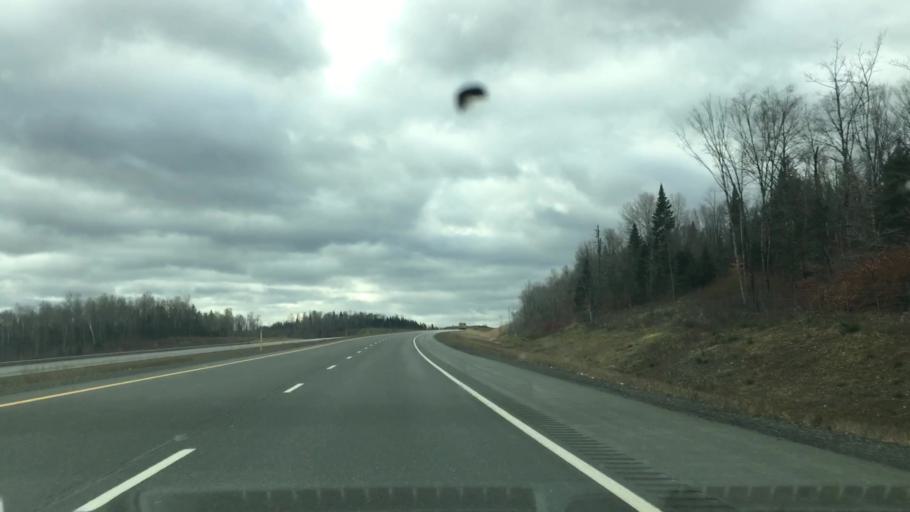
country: US
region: Maine
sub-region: Aroostook County
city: Fort Fairfield
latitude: 46.6655
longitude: -67.7304
